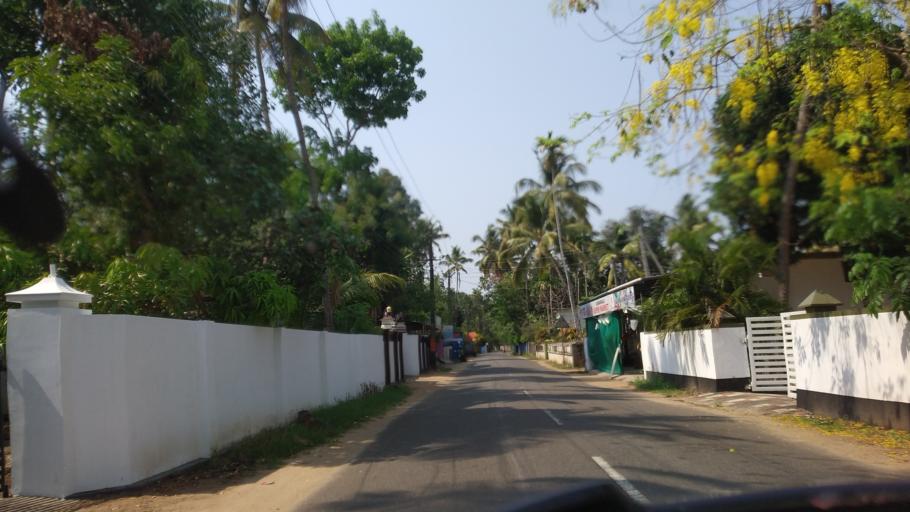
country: IN
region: Kerala
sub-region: Thrissur District
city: Thanniyam
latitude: 10.3529
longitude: 76.1126
